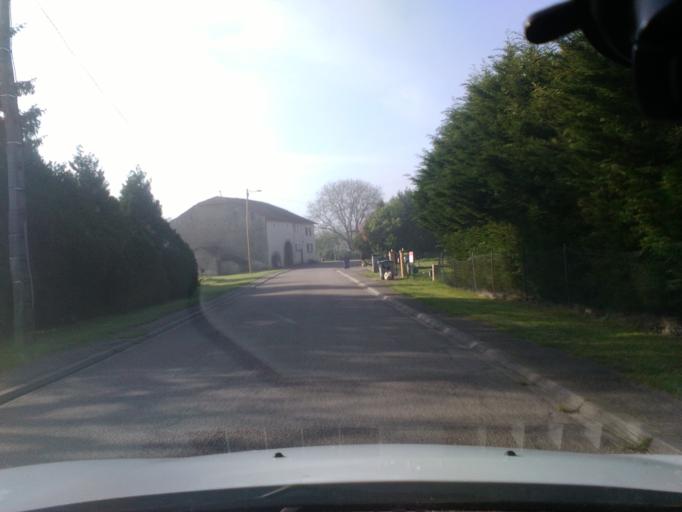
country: FR
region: Lorraine
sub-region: Departement des Vosges
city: Charmes
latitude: 48.3358
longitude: 6.2360
